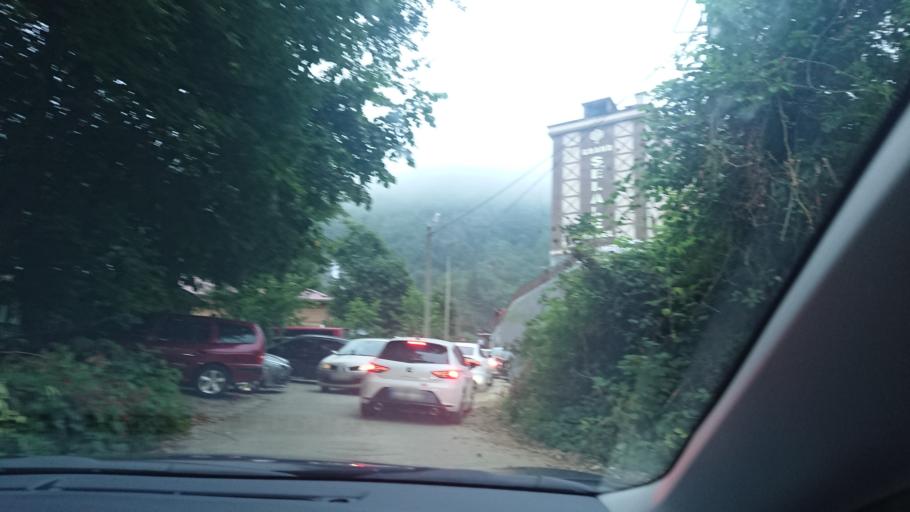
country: TR
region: Rize
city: Kaptanpasa
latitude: 41.0452
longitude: 40.8068
